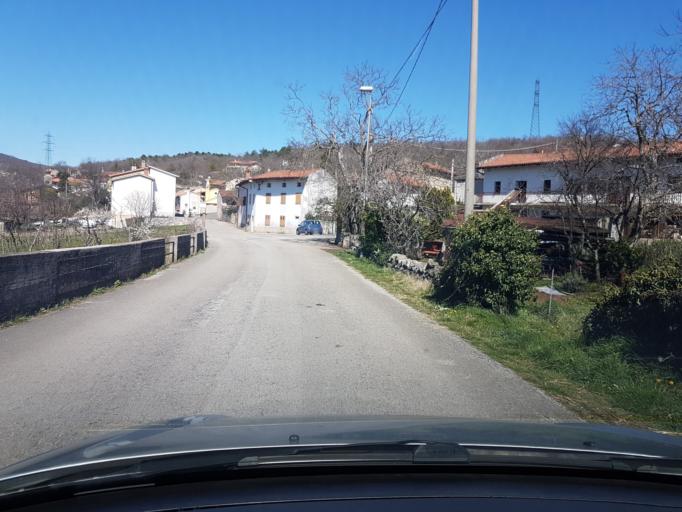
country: IT
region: Friuli Venezia Giulia
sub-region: Provincia di Trieste
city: Sistiana-Visogliano
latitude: 45.7873
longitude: 13.6447
